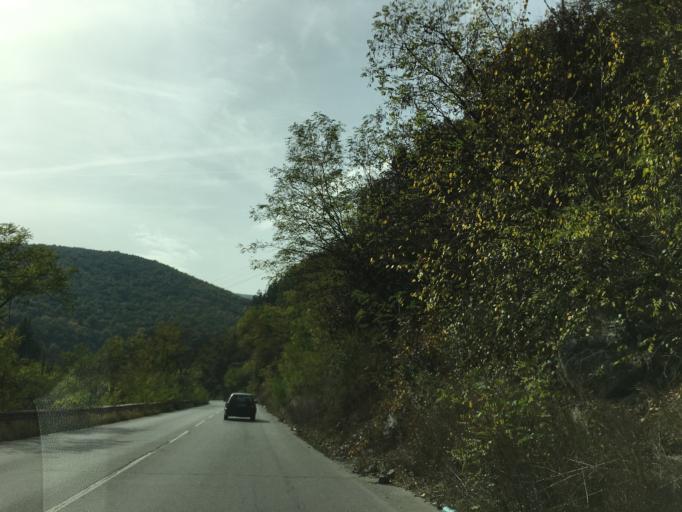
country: BG
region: Sofia-Capital
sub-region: Stolichna Obshtina
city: Sofia
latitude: 42.5710
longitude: 23.4325
